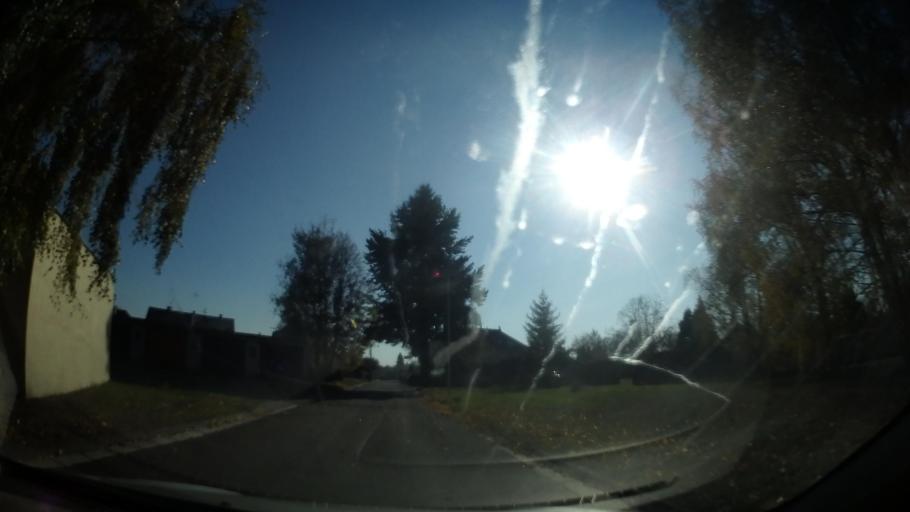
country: CZ
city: Tyniste nad Orlici
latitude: 50.1576
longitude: 16.0675
